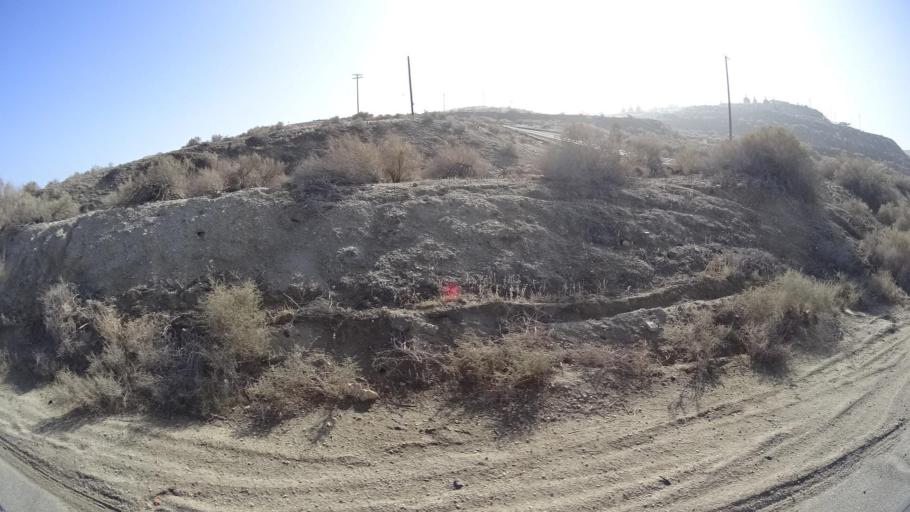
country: US
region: California
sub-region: Kern County
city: Taft Heights
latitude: 35.1389
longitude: -119.5027
